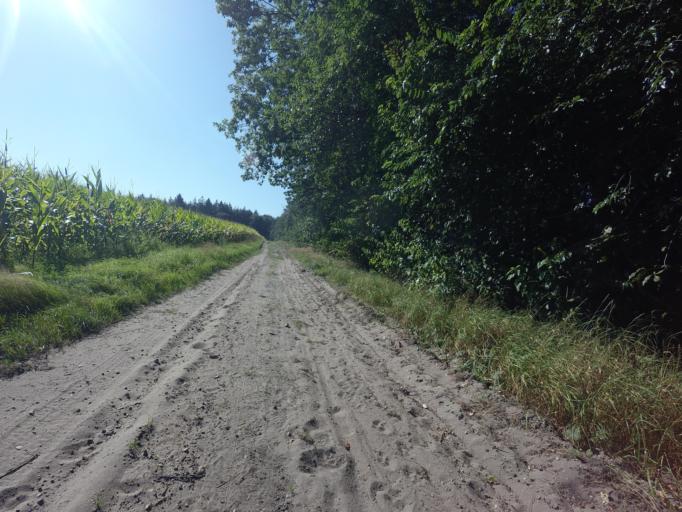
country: DE
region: Lower Saxony
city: Wielen
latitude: 52.5449
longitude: 6.7167
